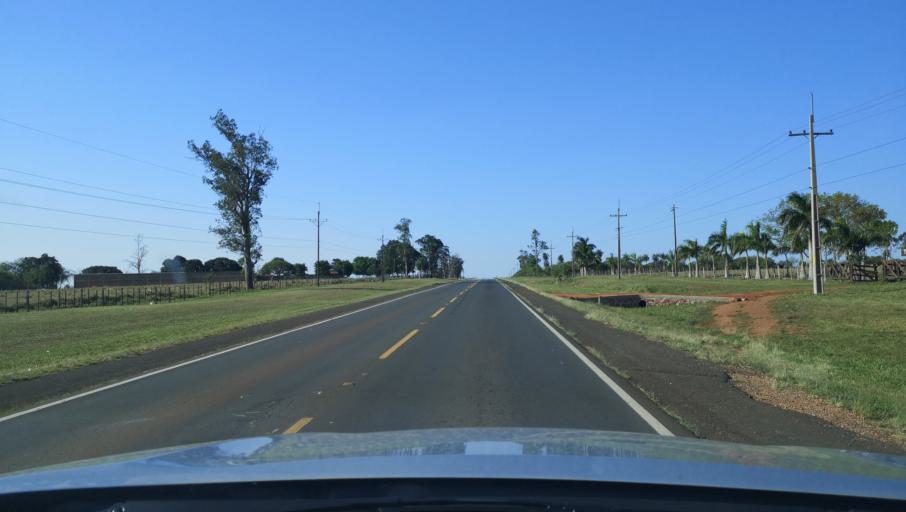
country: PY
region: Misiones
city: Santa Maria
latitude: -26.8261
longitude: -57.0290
